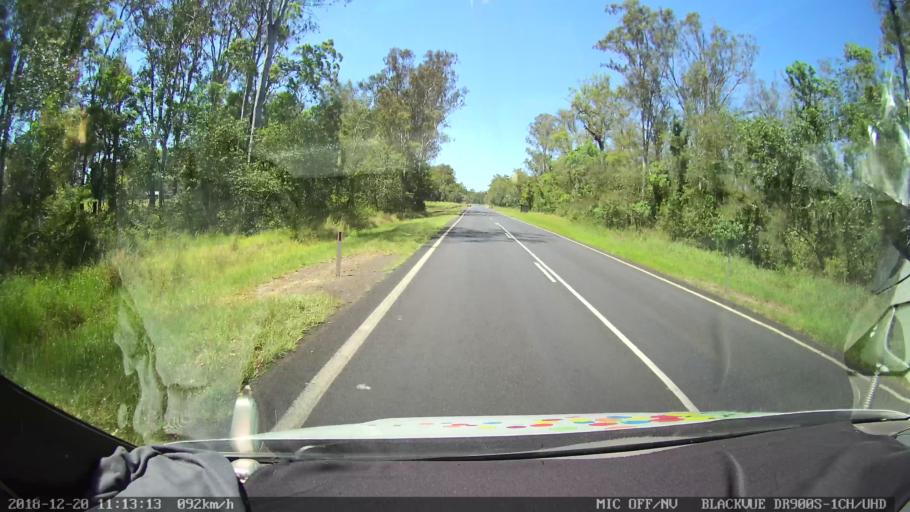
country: AU
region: New South Wales
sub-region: Richmond Valley
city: Casino
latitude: -28.9847
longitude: 153.0098
